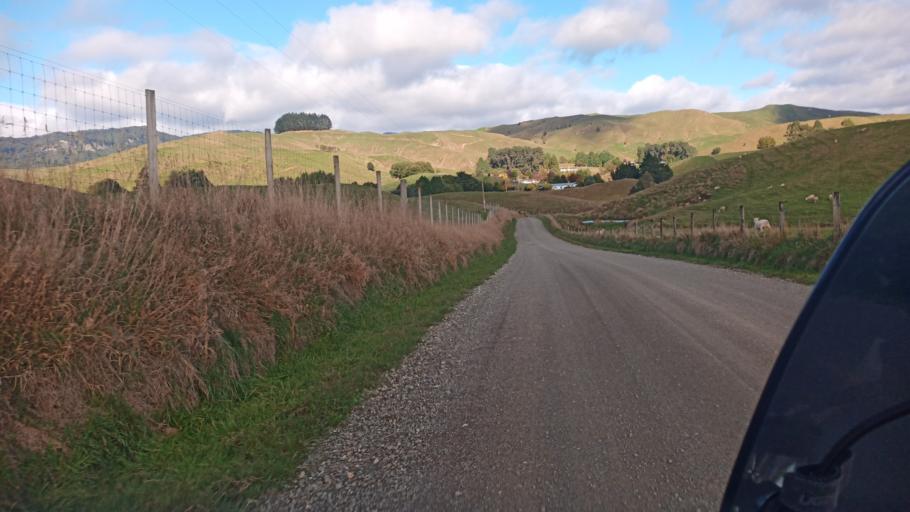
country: NZ
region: Bay of Plenty
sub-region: Opotiki District
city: Opotiki
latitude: -38.4578
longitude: 177.3909
